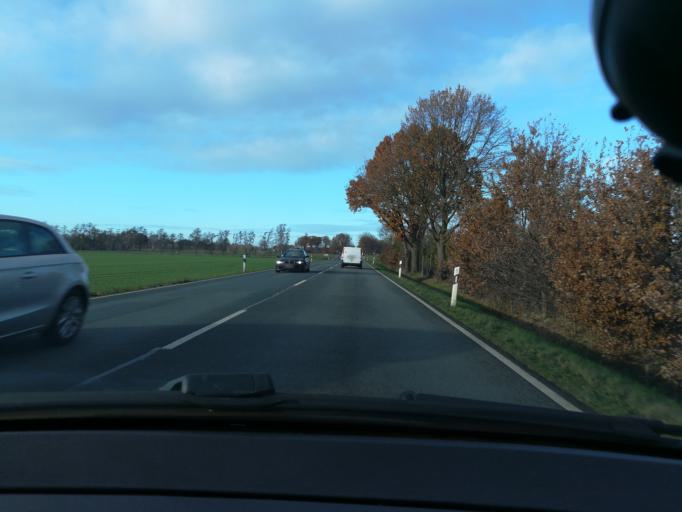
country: DE
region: Lower Saxony
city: Uchte
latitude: 52.5206
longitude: 8.8942
